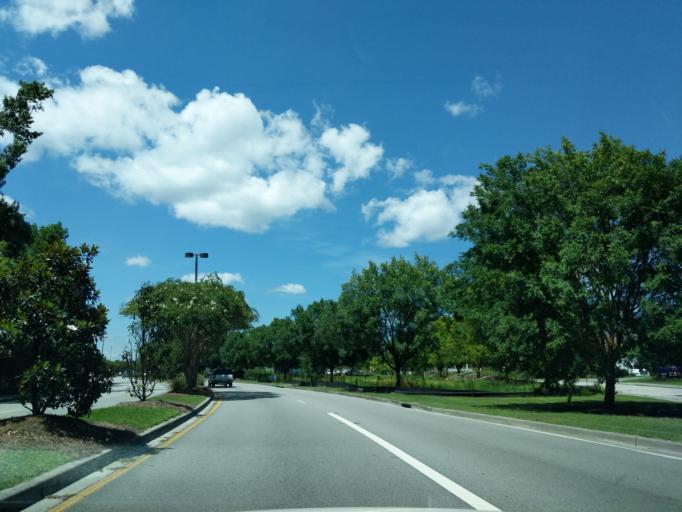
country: US
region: South Carolina
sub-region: Charleston County
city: North Charleston
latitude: 32.8707
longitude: -80.0152
